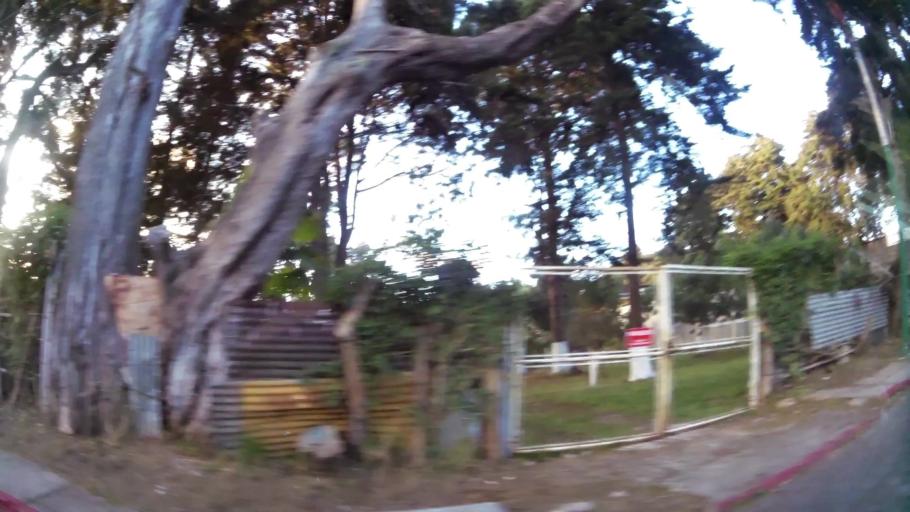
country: GT
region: Sacatepequez
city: San Lucas Sacatepequez
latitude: 14.6135
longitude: -90.6585
